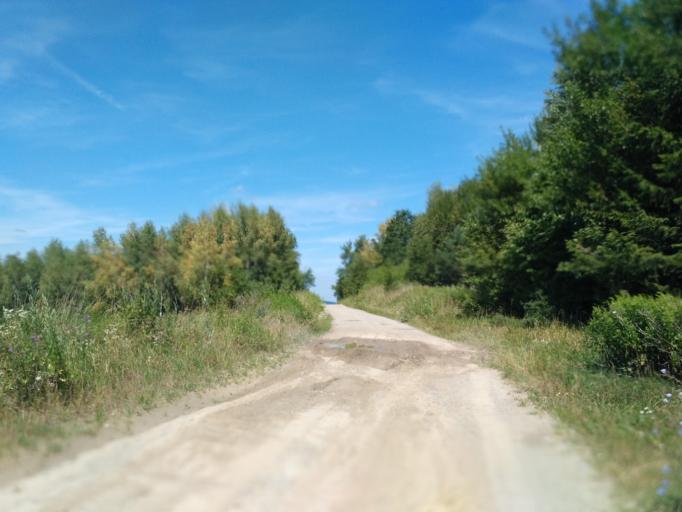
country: PL
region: Subcarpathian Voivodeship
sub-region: Powiat sanocki
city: Bukowsko
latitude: 49.4986
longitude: 22.0947
